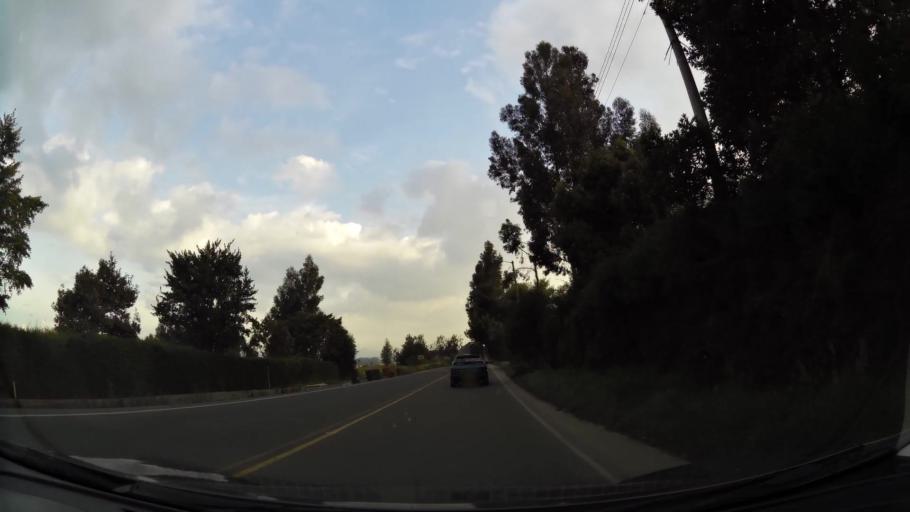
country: CO
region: Cundinamarca
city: Cota
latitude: 4.8228
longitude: -74.0892
